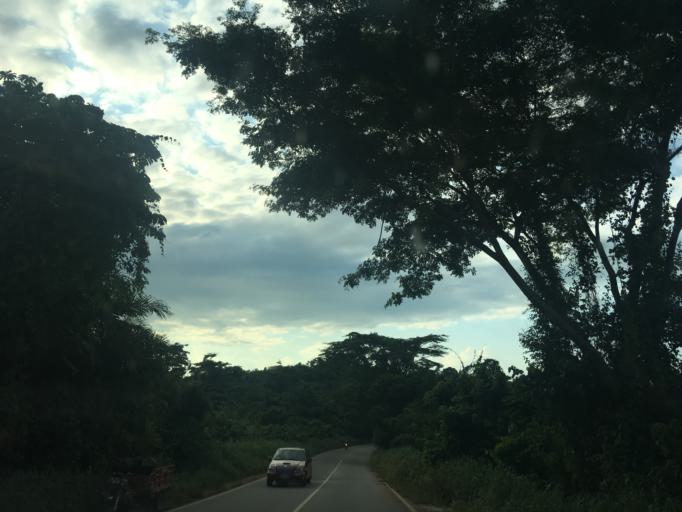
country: GH
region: Western
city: Bibiani
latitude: 6.4117
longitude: -2.3018
